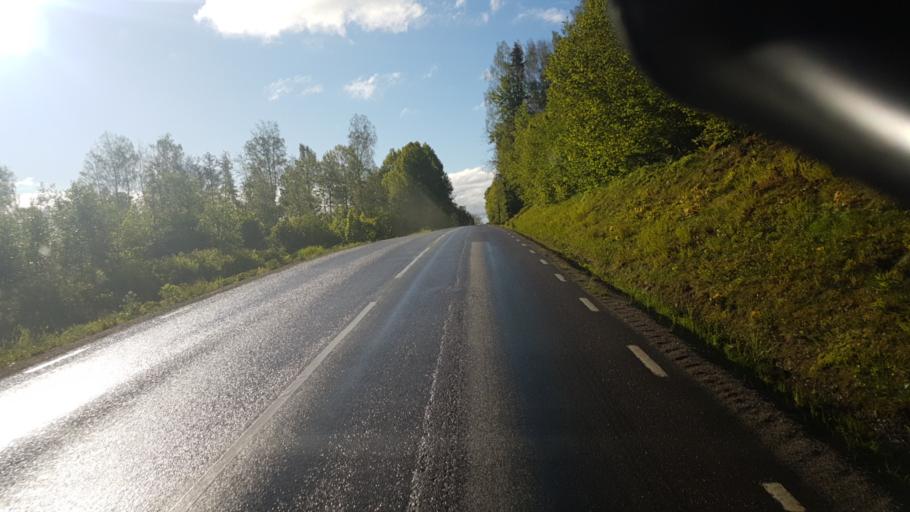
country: SE
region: Vaermland
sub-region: Eda Kommun
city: Amotfors
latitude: 59.6569
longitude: 12.4395
